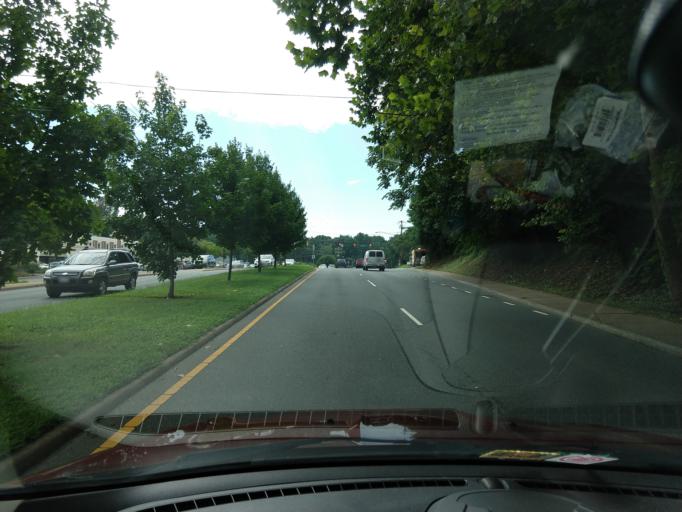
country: US
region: Virginia
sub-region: City of Charlottesville
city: Charlottesville
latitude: 38.0551
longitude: -78.5014
